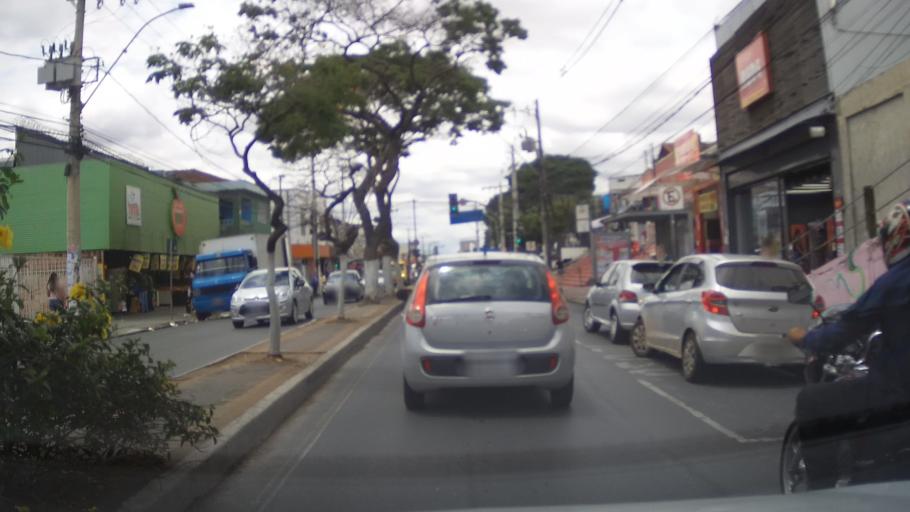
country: BR
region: Minas Gerais
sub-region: Belo Horizonte
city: Belo Horizonte
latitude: -19.8158
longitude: -43.9571
